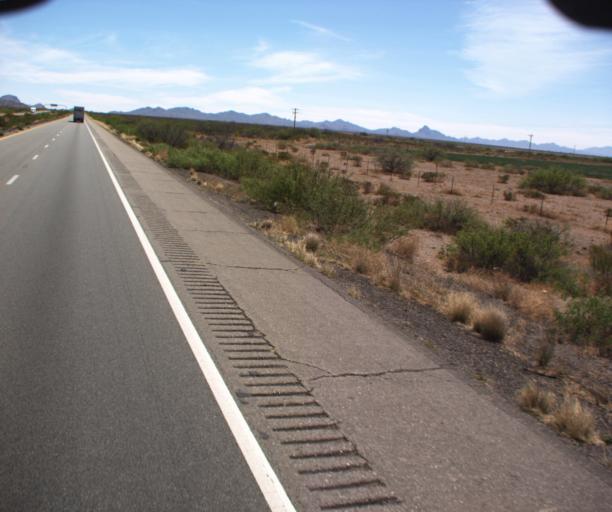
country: US
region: New Mexico
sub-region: Hidalgo County
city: Lordsburg
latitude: 32.2522
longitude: -109.1565
